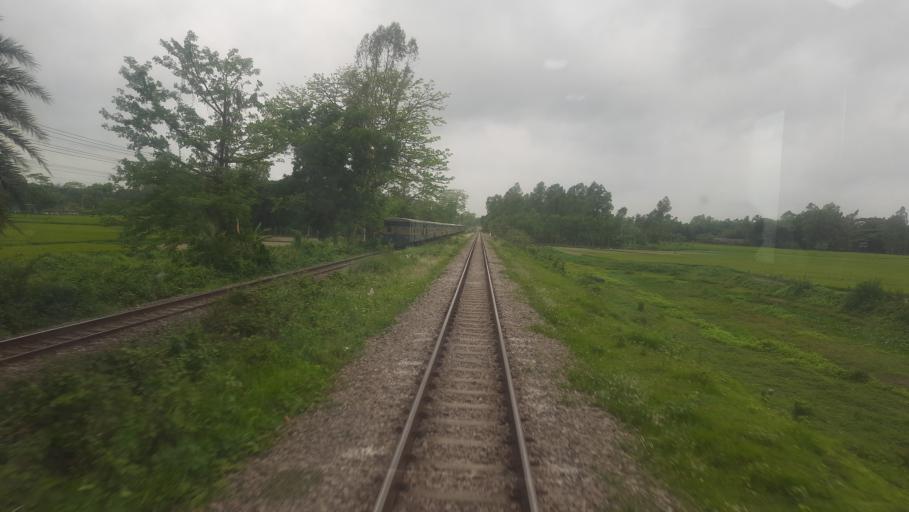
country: BD
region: Dhaka
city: Narsingdi
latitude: 23.9431
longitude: 90.7843
